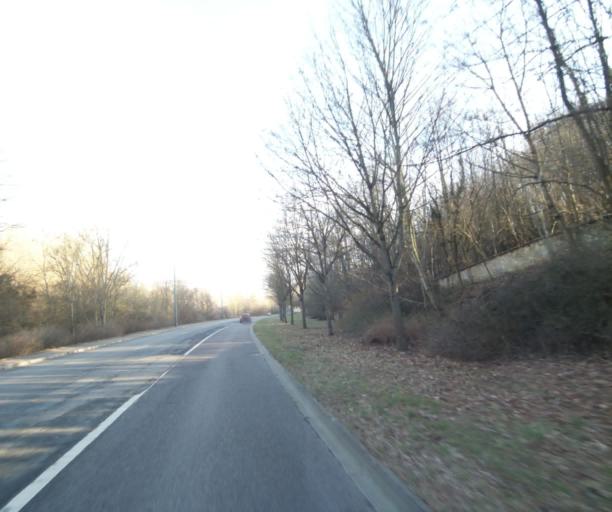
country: FR
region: Lorraine
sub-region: Departement de Meurthe-et-Moselle
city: Villers-les-Nancy
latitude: 48.6639
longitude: 6.1429
